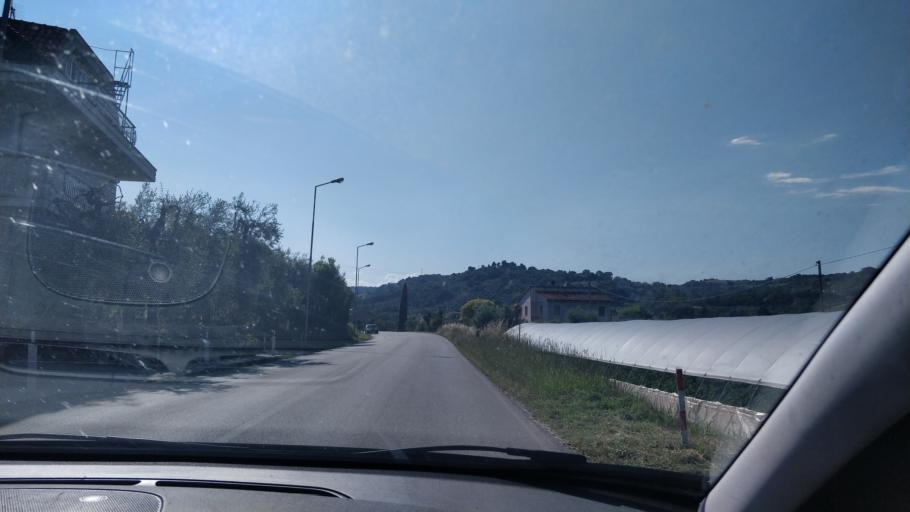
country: IT
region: The Marches
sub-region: Provincia di Ascoli Piceno
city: Cupra Marittima
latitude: 43.0363
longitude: 13.8352
